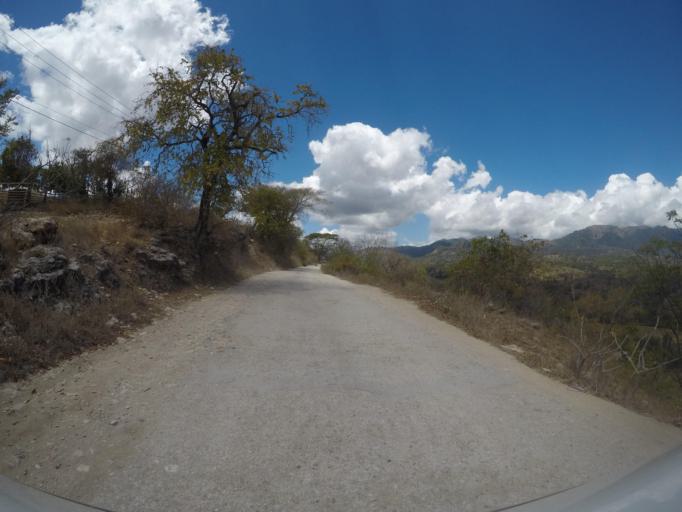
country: TL
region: Baucau
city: Baucau
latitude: -8.4854
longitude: 126.6159
